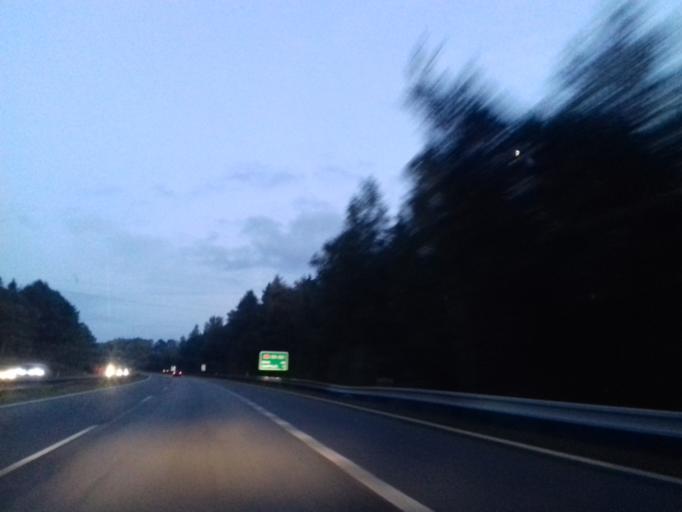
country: CZ
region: Vysocina
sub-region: Okres Pelhrimov
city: Zeliv
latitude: 49.5746
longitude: 15.2690
